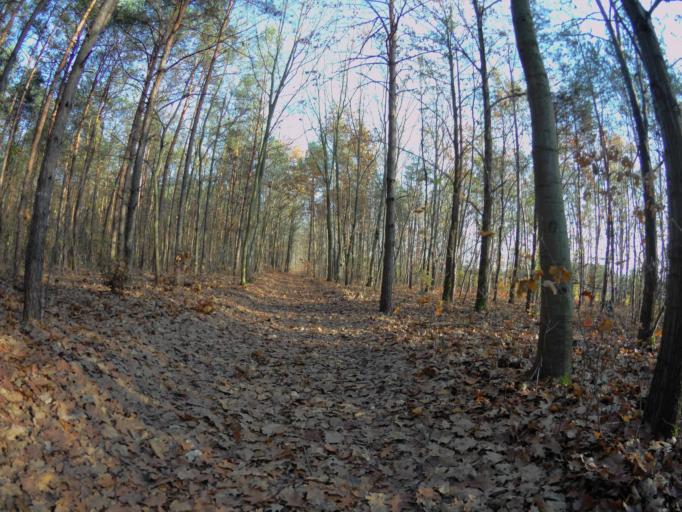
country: PL
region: Subcarpathian Voivodeship
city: Nowa Sarzyna
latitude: 50.3046
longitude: 22.3584
